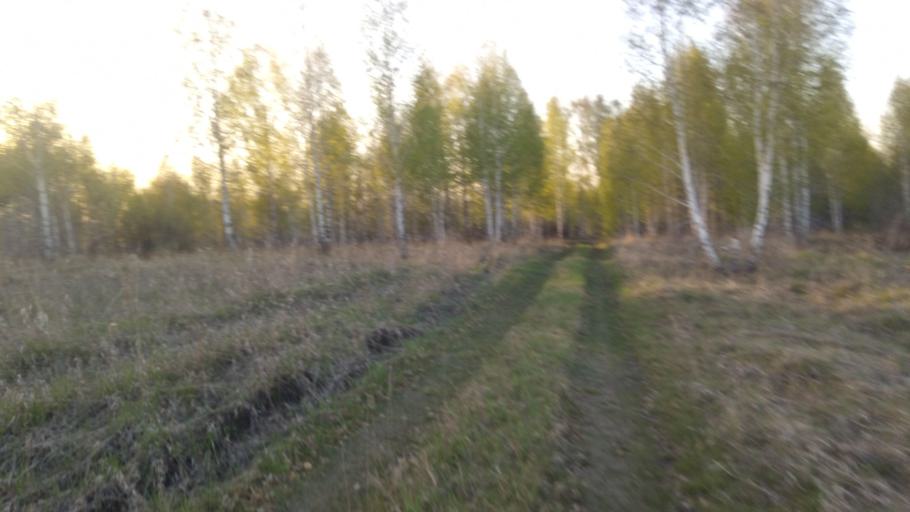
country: RU
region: Chelyabinsk
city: Timiryazevskiy
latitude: 54.9917
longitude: 60.8522
